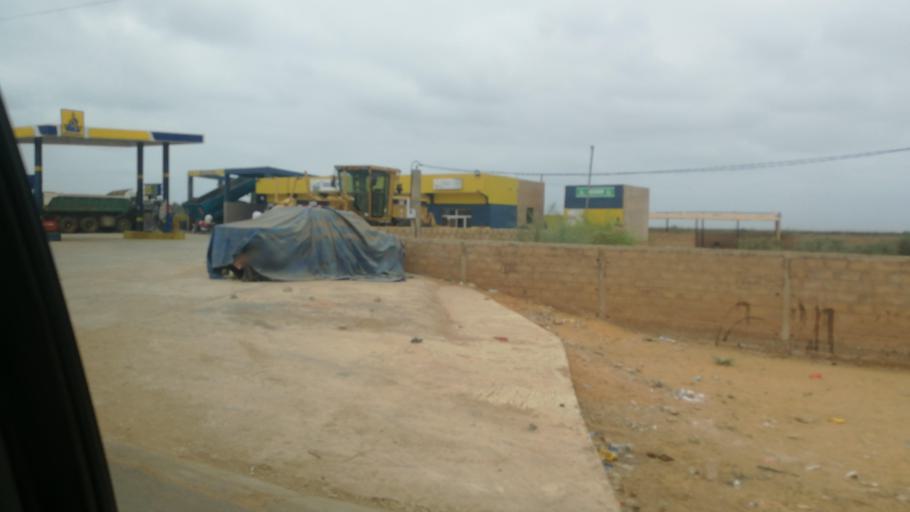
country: SN
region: Saint-Louis
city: Rosso
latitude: 16.2763
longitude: -16.1479
